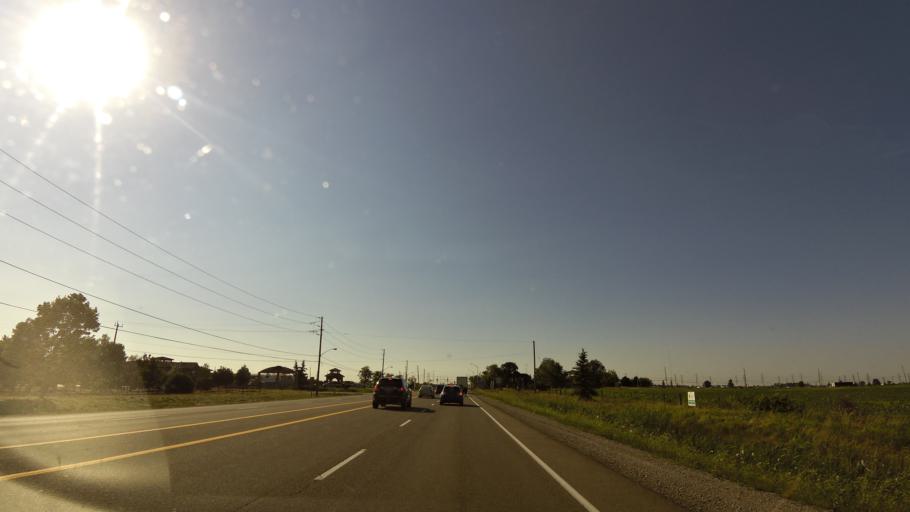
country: CA
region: Ontario
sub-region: Halton
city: Milton
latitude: 43.5533
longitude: -79.8053
